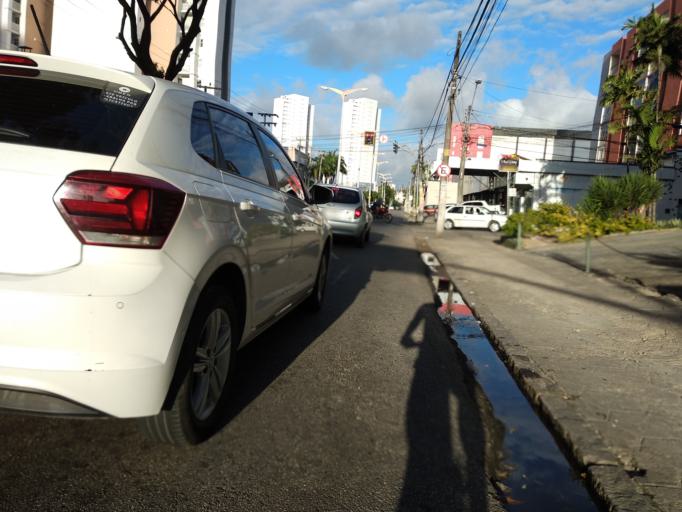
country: BR
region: Ceara
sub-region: Fortaleza
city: Fortaleza
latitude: -3.7353
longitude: -38.5192
